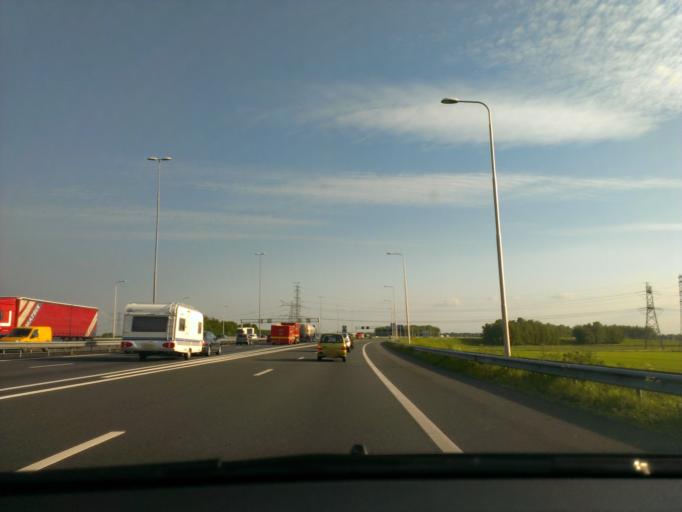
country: NL
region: Gelderland
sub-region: Gemeente Overbetuwe
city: Valburg
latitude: 51.9163
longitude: 5.7718
